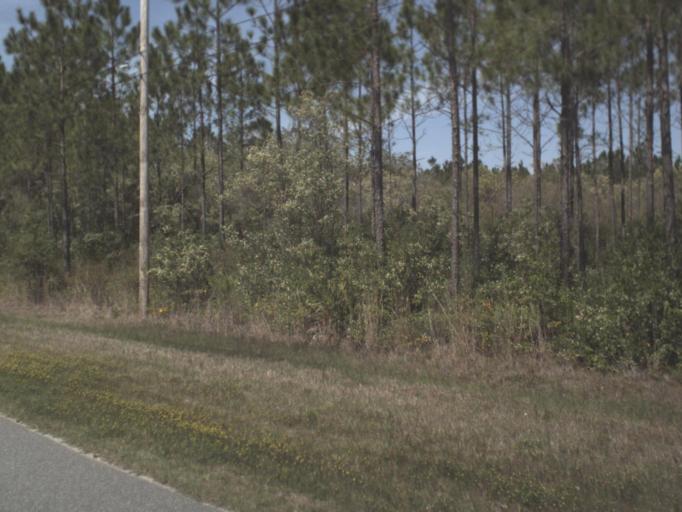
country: US
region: Florida
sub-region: Bay County
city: Lynn Haven
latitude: 30.3290
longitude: -85.7269
